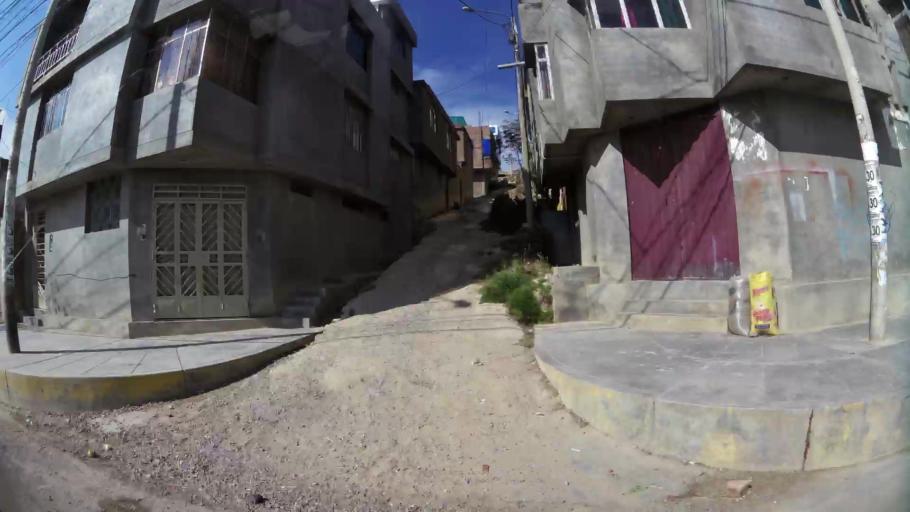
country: PE
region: Junin
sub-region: Provincia de Huancayo
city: Huancayo
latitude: -12.0580
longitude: -75.1915
